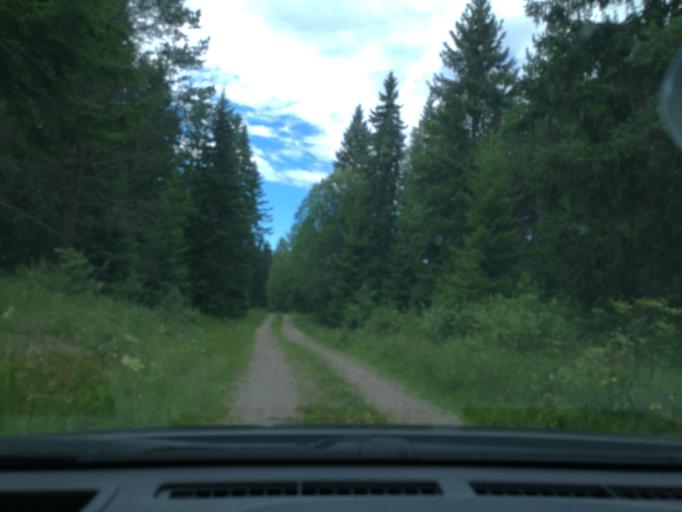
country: SE
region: Vaestmanland
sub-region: Surahammars Kommun
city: Ramnas
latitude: 59.8104
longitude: 16.3220
